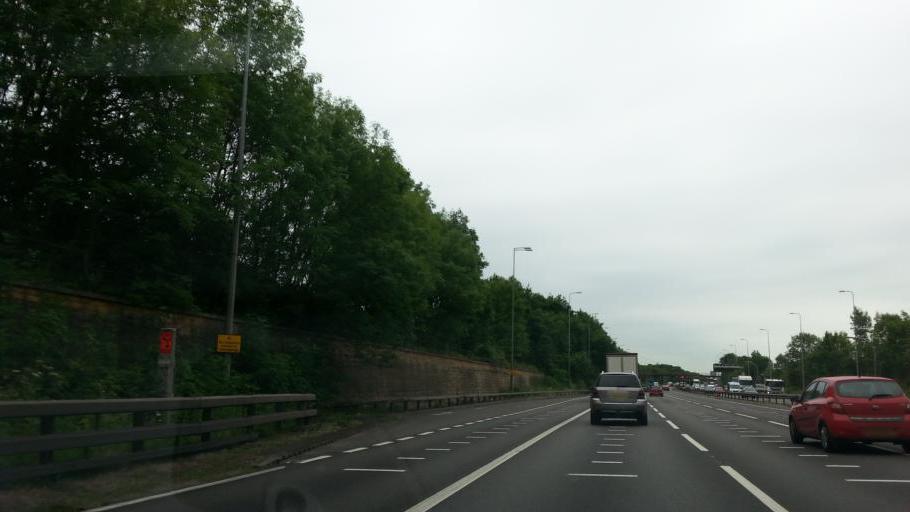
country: GB
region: England
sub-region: Solihull
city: Solihull
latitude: 52.3981
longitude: -1.7623
